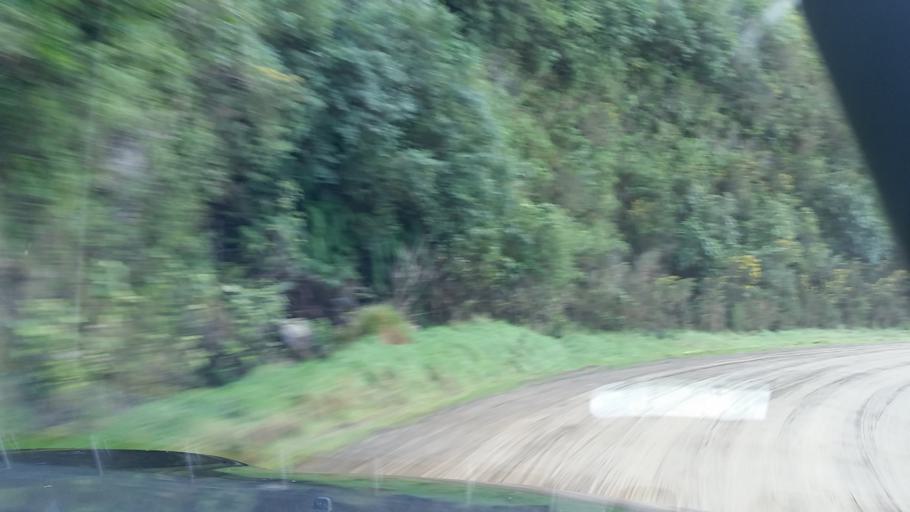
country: NZ
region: Marlborough
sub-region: Marlborough District
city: Picton
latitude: -40.9859
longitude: 173.8149
